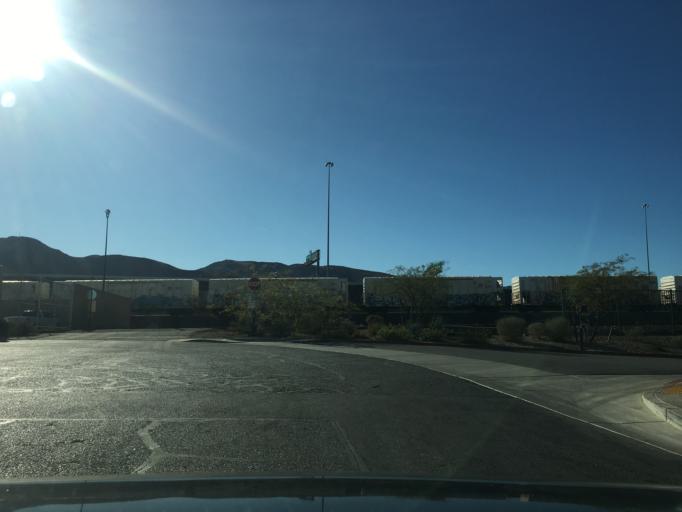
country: US
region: Nevada
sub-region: Clark County
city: Henderson
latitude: 36.0345
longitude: -115.0208
